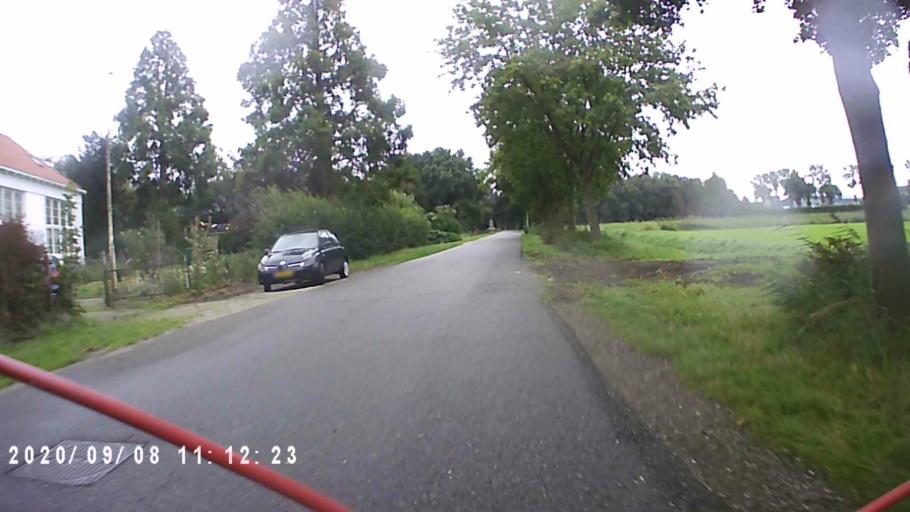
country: NL
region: Groningen
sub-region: Gemeente Hoogezand-Sappemeer
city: Hoogezand
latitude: 53.1771
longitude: 6.7126
